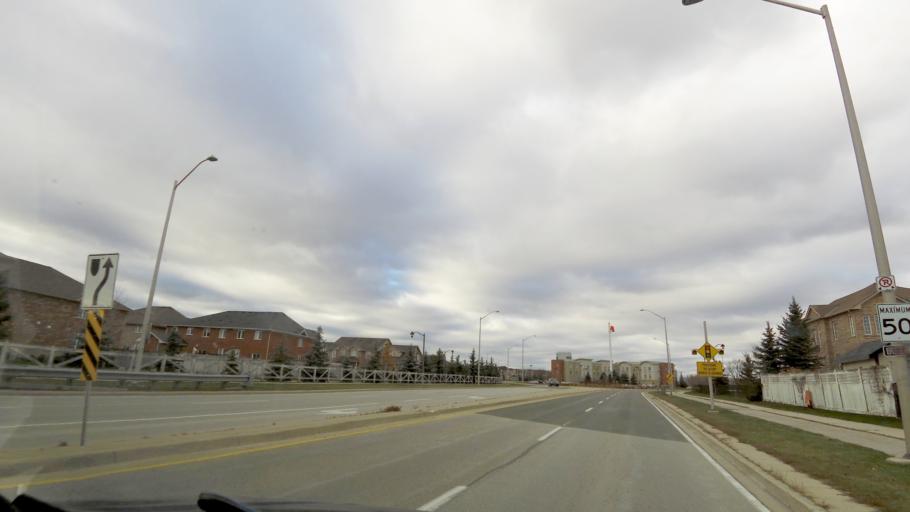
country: CA
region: Ontario
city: Oakville
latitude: 43.4451
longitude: -79.7536
